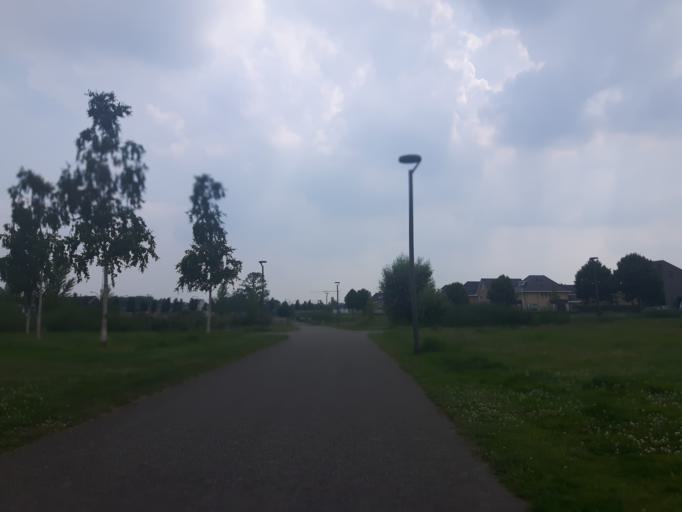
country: NL
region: Overijssel
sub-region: Gemeente Borne
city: Borne
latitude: 52.2968
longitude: 6.7693
